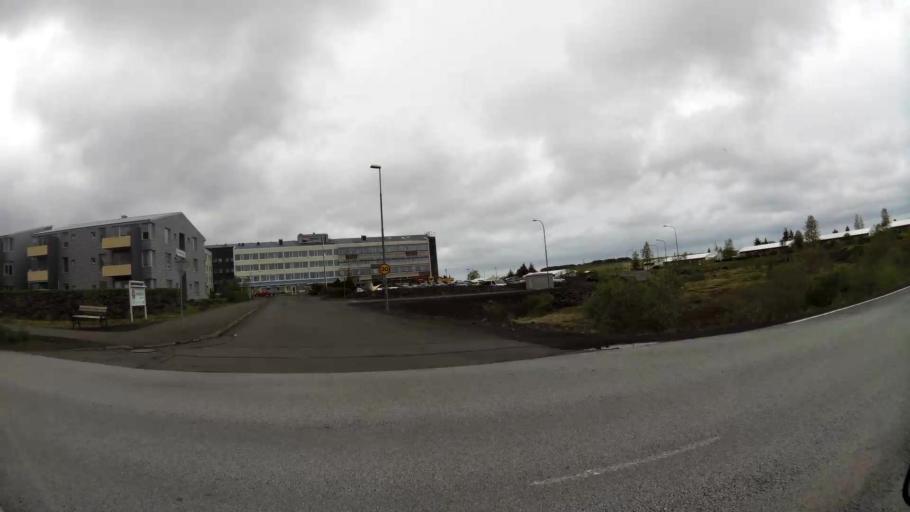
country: IS
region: Capital Region
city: Hafnarfjoerdur
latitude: 64.0799
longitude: -21.9712
